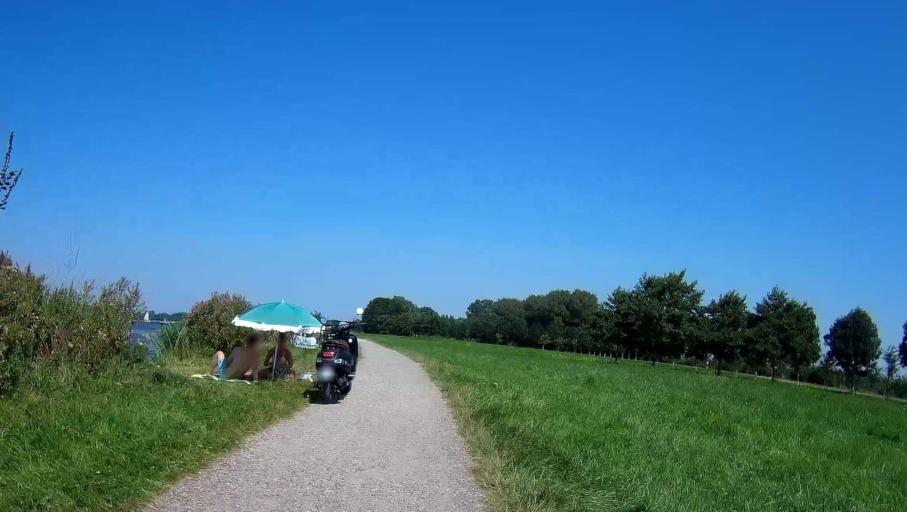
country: NL
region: South Holland
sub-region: Gemeente Voorschoten
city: Voorschoten
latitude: 52.1082
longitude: 4.4549
